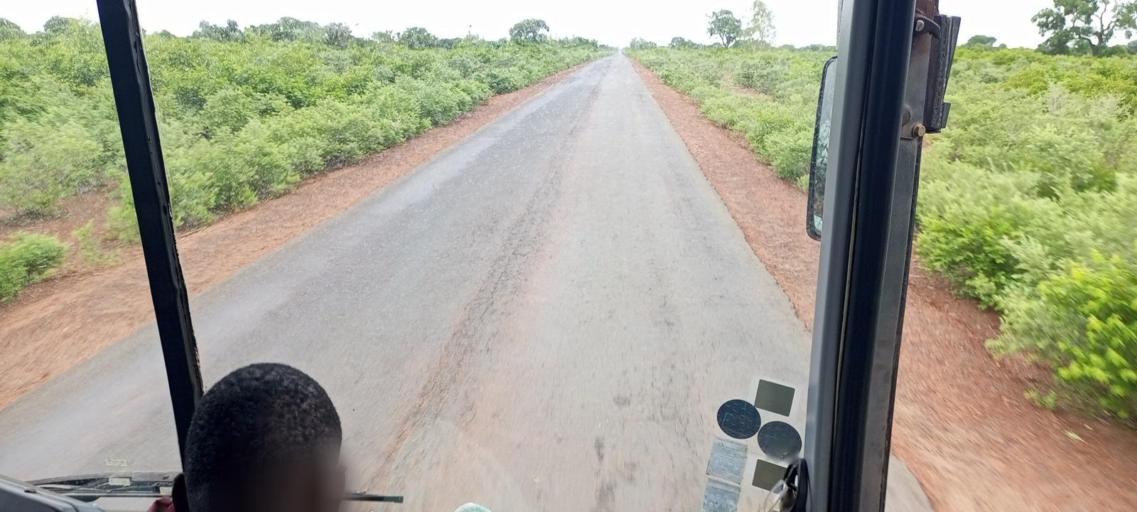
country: ML
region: Sikasso
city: Koutiala
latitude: 12.5617
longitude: -5.5940
